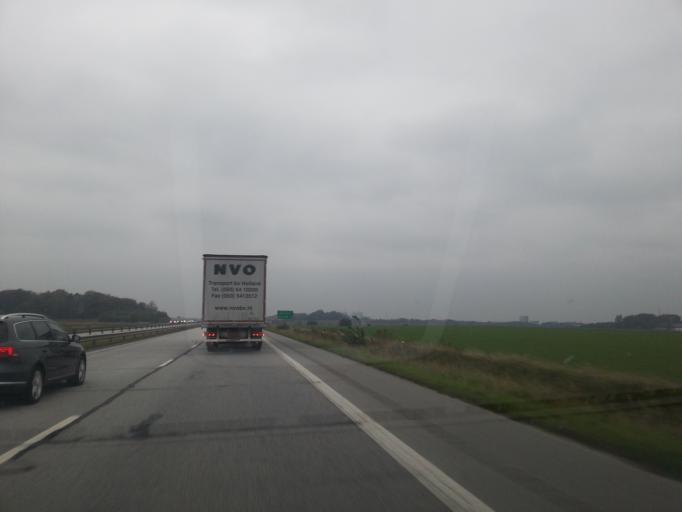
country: SE
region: Skane
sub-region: Malmo
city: Tygelsjo
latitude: 55.5391
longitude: 13.0062
